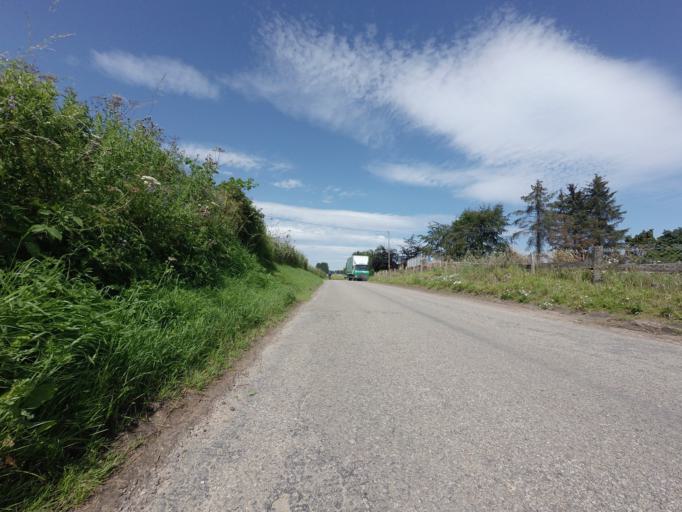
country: GB
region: Scotland
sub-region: Highland
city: Inverness
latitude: 57.5260
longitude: -4.3170
